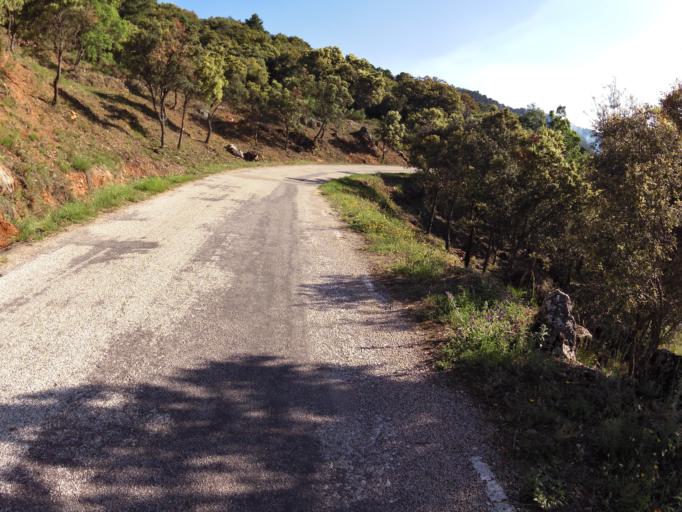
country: ES
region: Castille-La Mancha
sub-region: Provincia de Albacete
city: Riopar
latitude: 38.5174
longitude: -2.4566
